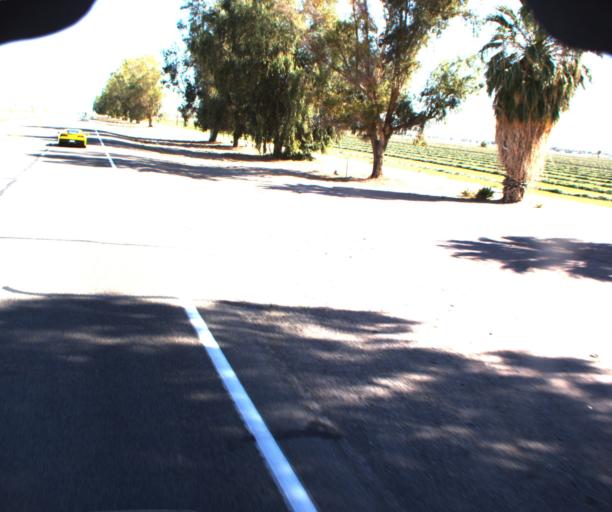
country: US
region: California
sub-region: San Bernardino County
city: Needles
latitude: 34.8732
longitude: -114.5977
